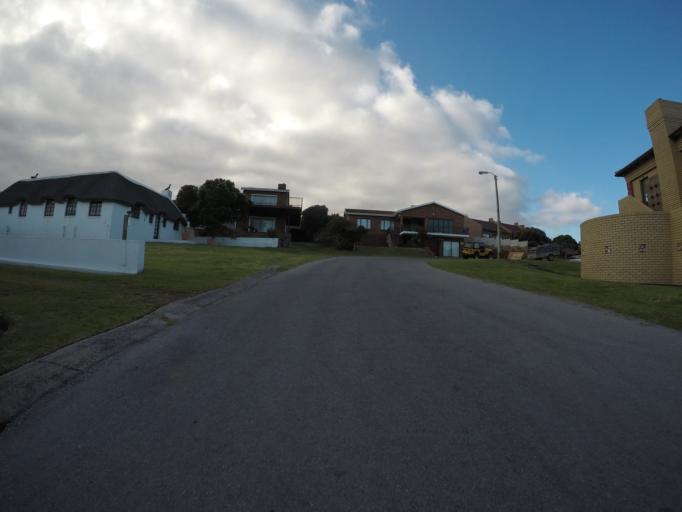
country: ZA
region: Western Cape
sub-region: Eden District Municipality
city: Riversdale
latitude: -34.4247
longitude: 21.3415
